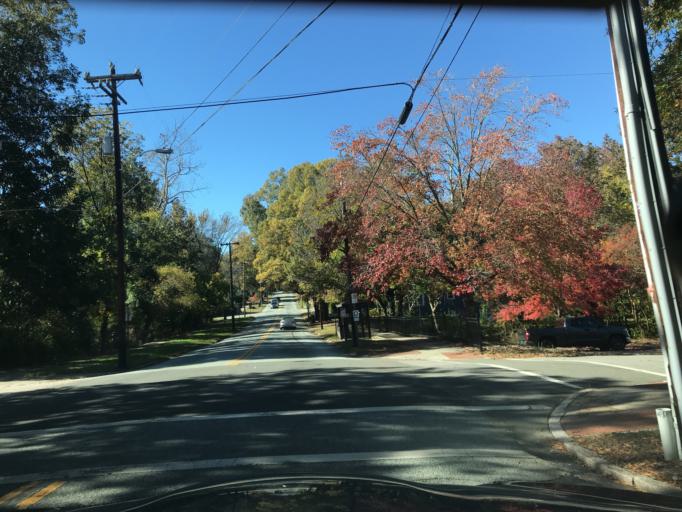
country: US
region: North Carolina
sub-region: Durham County
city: Durham
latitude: 36.0170
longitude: -78.9139
